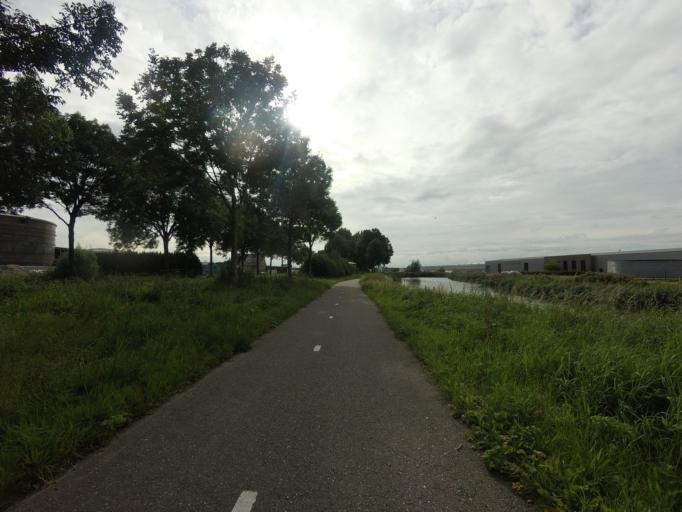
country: NL
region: North Holland
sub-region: Gemeente Medemblik
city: Medemblik
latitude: 52.7236
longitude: 5.1906
